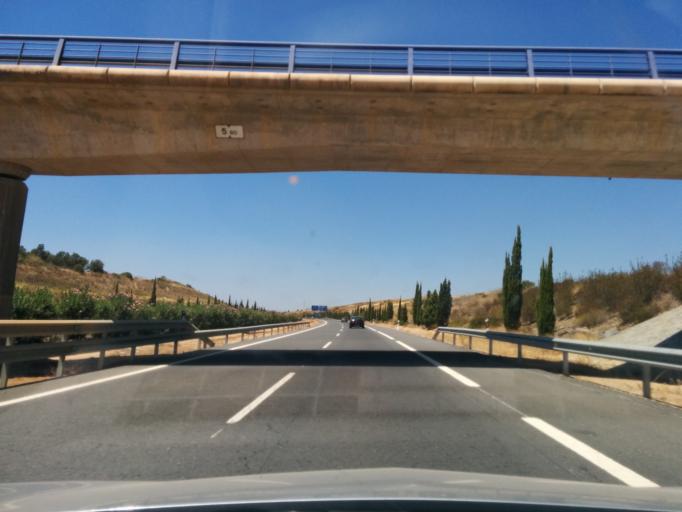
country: ES
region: Andalusia
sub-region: Provincia de Huelva
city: Gibraleon
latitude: 37.3551
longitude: -6.9388
